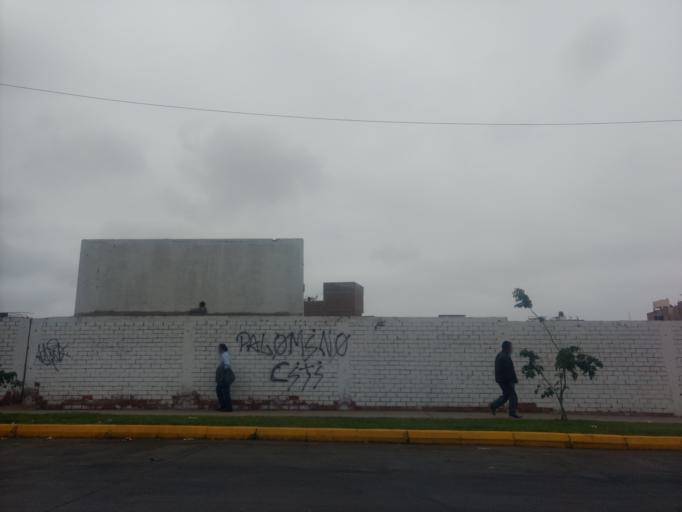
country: PE
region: Callao
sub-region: Callao
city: Callao
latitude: -12.0610
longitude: -77.0817
